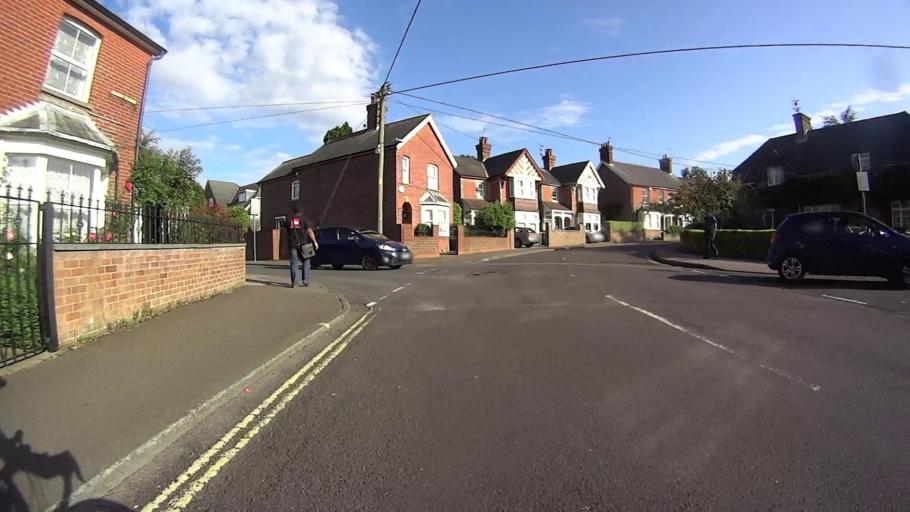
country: GB
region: England
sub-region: West Sussex
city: Crawley
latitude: 51.1087
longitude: -0.1876
